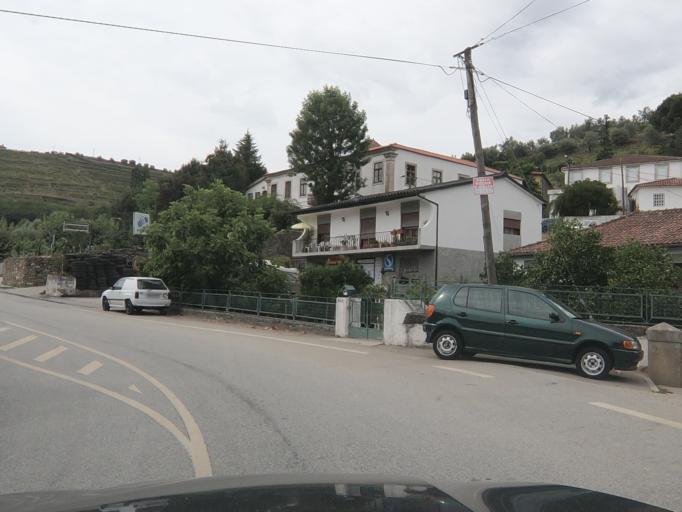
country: PT
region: Vila Real
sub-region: Santa Marta de Penaguiao
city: Santa Marta de Penaguiao
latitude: 41.2186
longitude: -7.7824
